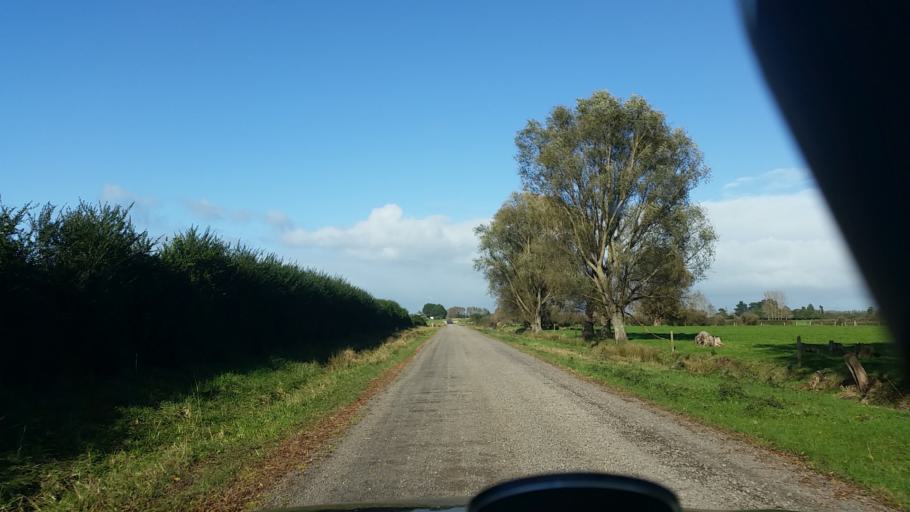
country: NZ
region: Bay of Plenty
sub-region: Western Bay of Plenty District
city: Katikati
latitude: -37.5895
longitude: 175.7132
